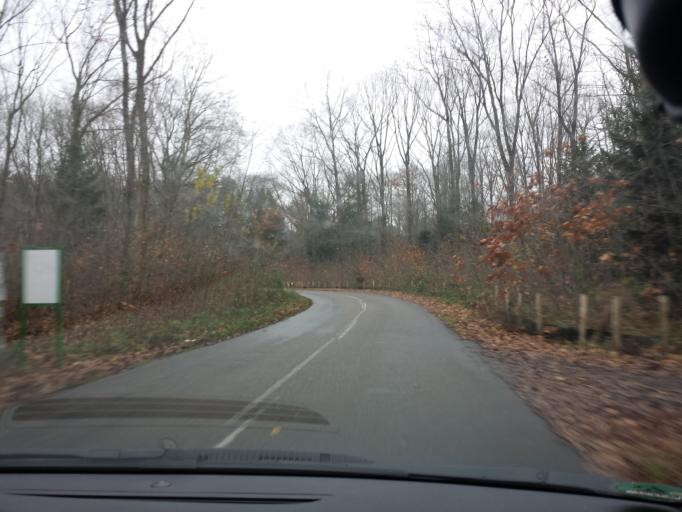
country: NL
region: Limburg
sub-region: Gemeente Brunssum
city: Brunssum
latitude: 50.9309
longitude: 6.0056
